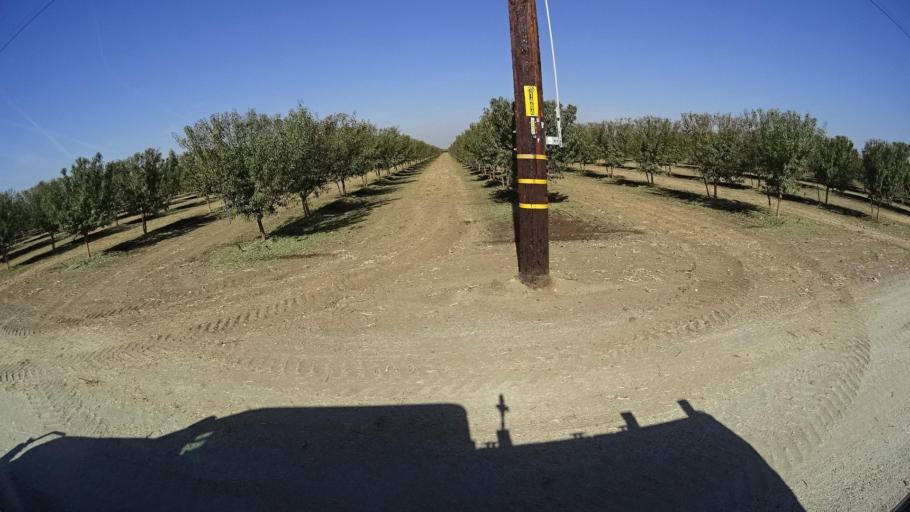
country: US
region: California
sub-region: Kern County
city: McFarland
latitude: 35.7033
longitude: -119.2027
